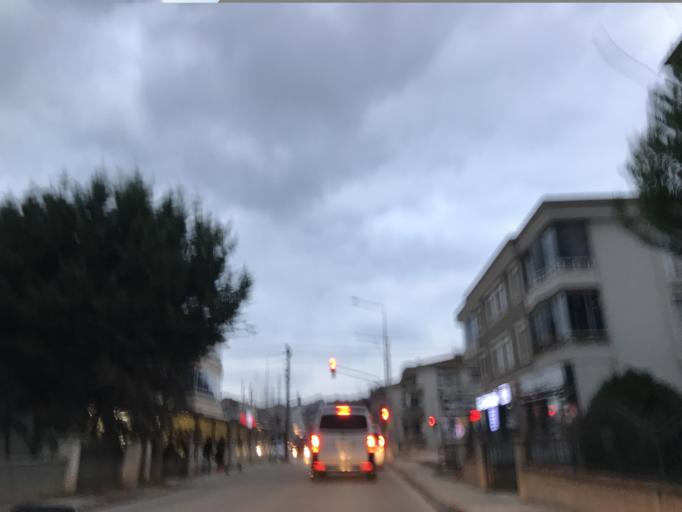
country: TR
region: Yalova
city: Yalova
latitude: 40.6413
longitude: 29.2592
